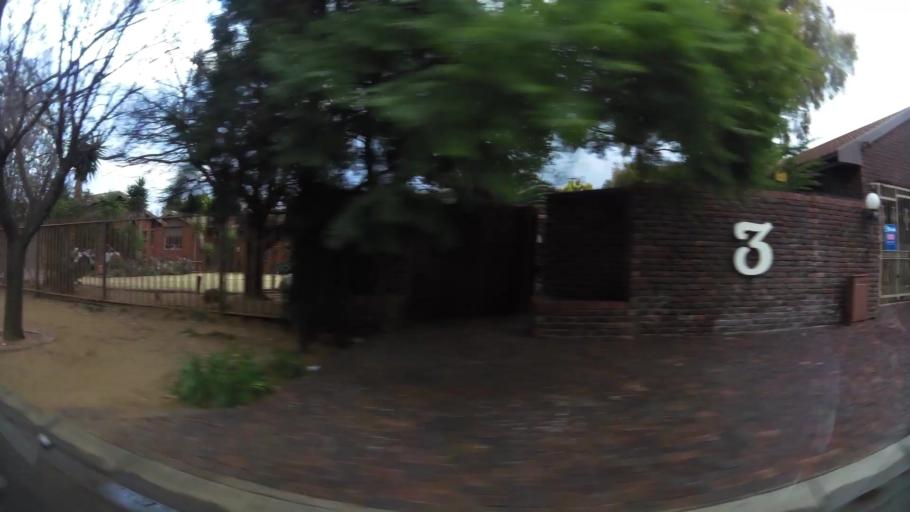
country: ZA
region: Orange Free State
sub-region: Lejweleputswa District Municipality
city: Welkom
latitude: -27.9513
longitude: 26.7277
